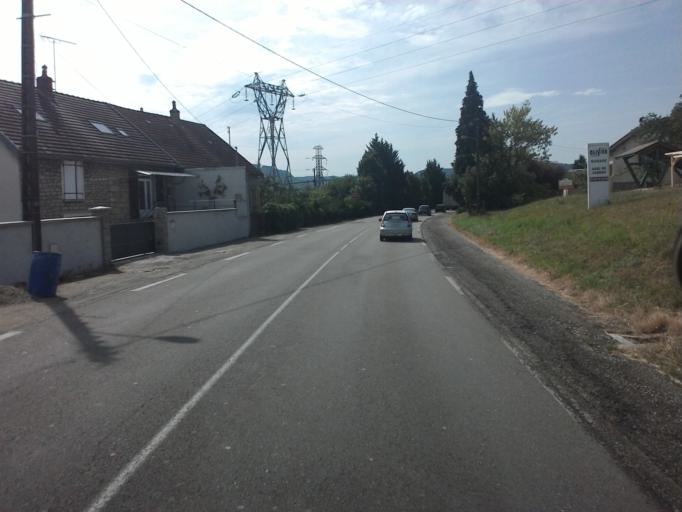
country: FR
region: Franche-Comte
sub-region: Departement du Jura
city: Lons-le-Saunier
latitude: 46.6925
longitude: 5.5604
